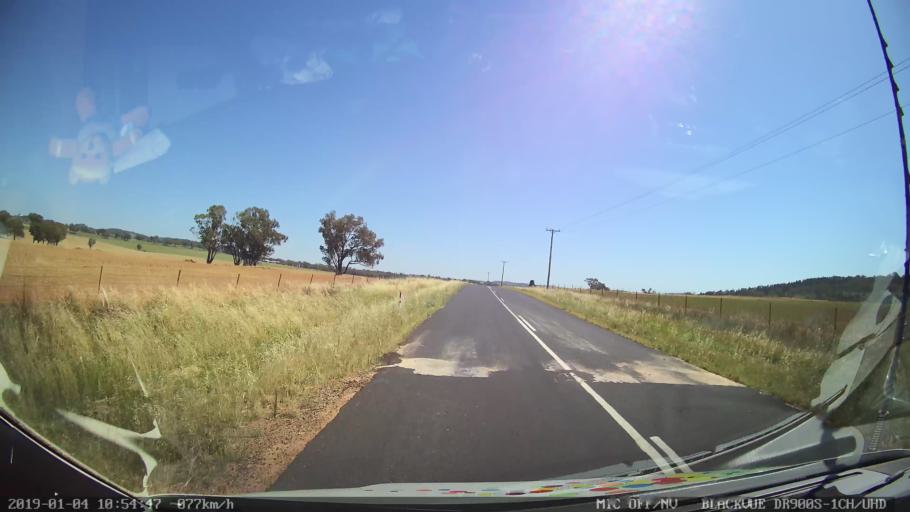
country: AU
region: New South Wales
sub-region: Cabonne
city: Molong
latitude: -33.2011
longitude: 148.6904
